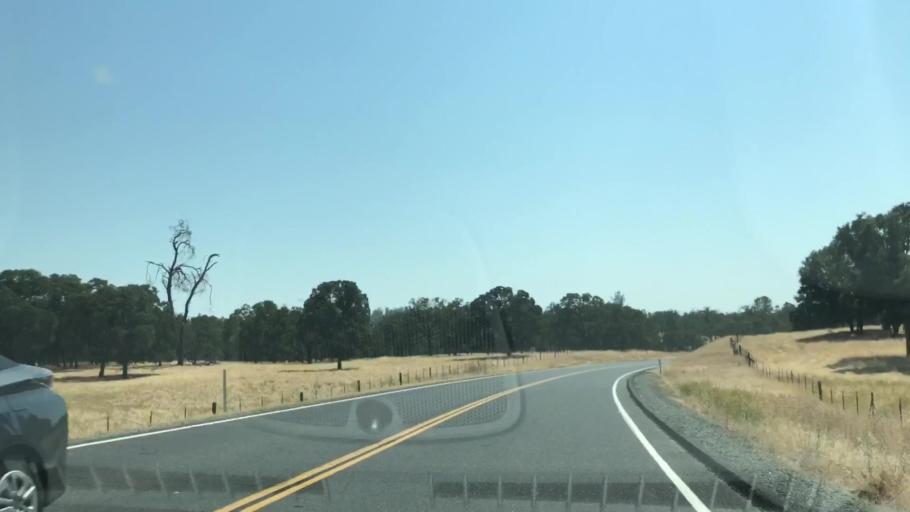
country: US
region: California
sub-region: Calaveras County
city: Copperopolis
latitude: 37.9585
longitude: -120.6135
